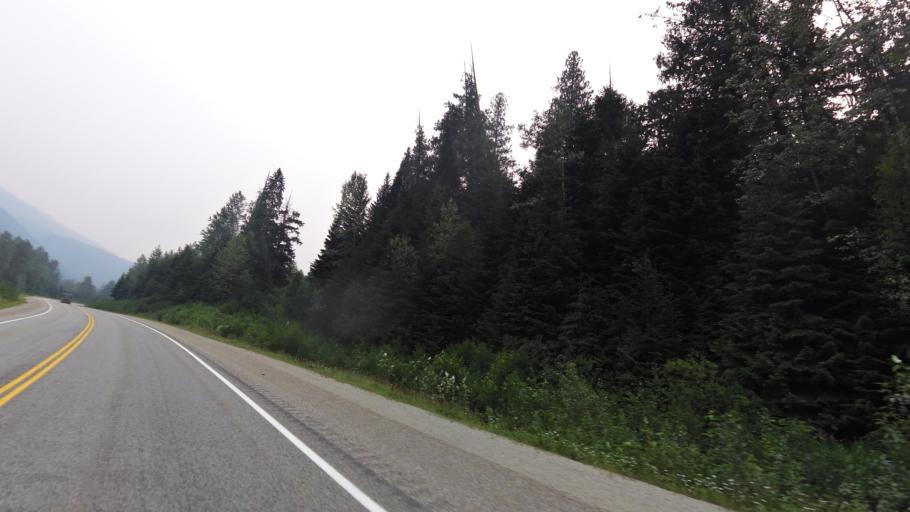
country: CA
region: Alberta
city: Jasper Park Lodge
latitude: 52.3321
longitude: -119.1782
